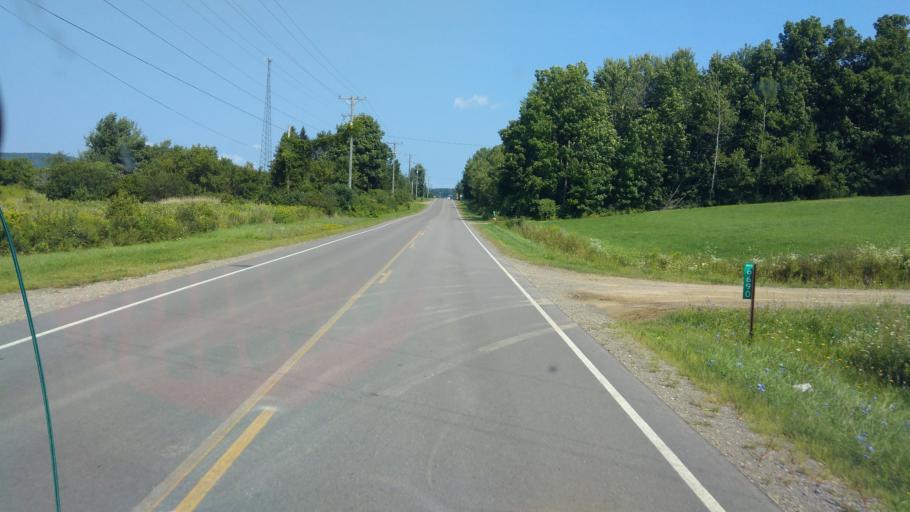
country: US
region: New York
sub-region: Allegany County
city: Belmont
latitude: 42.2923
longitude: -78.0262
